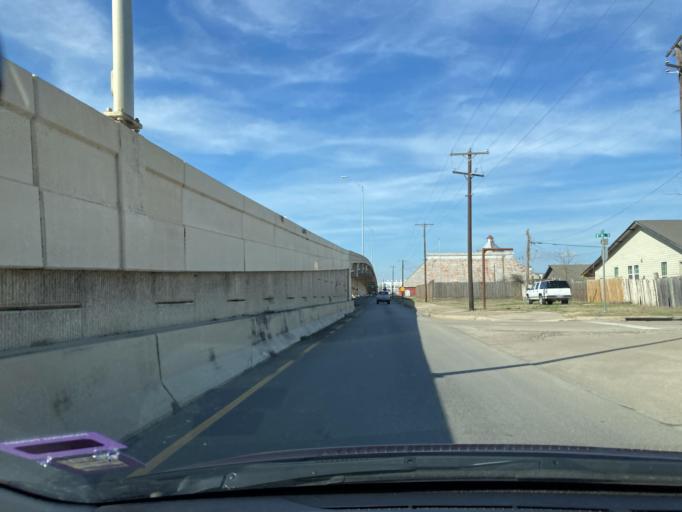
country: US
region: Texas
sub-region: Navarro County
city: Corsicana
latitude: 32.0912
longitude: -96.4574
